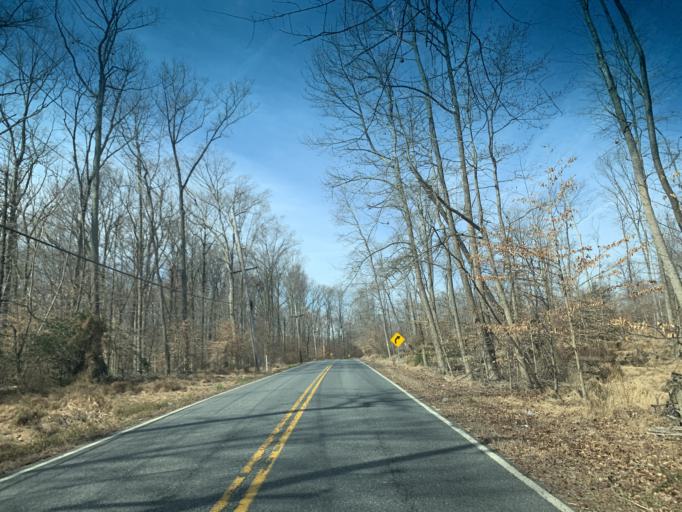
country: US
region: Maryland
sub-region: Cecil County
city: Charlestown
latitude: 39.5582
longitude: -76.0142
